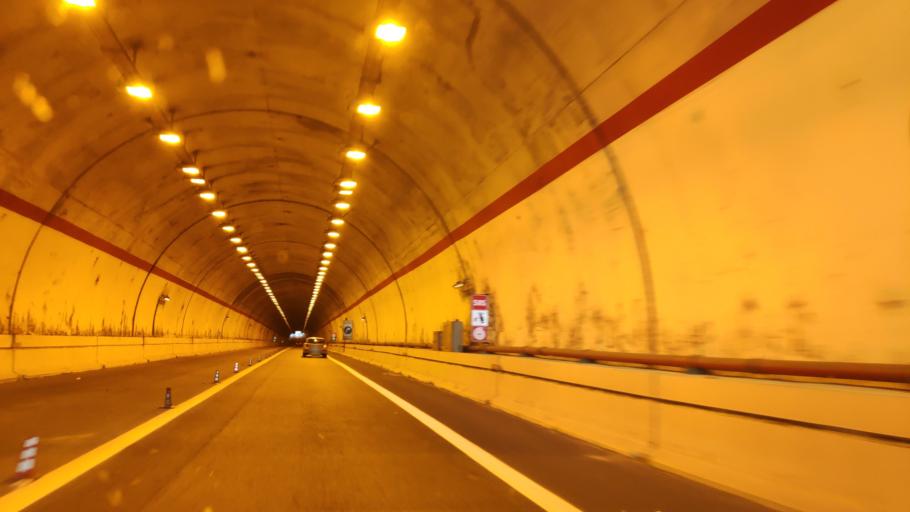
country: IT
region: Calabria
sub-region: Provincia di Reggio Calabria
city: Locri
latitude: 38.2414
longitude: 16.2426
